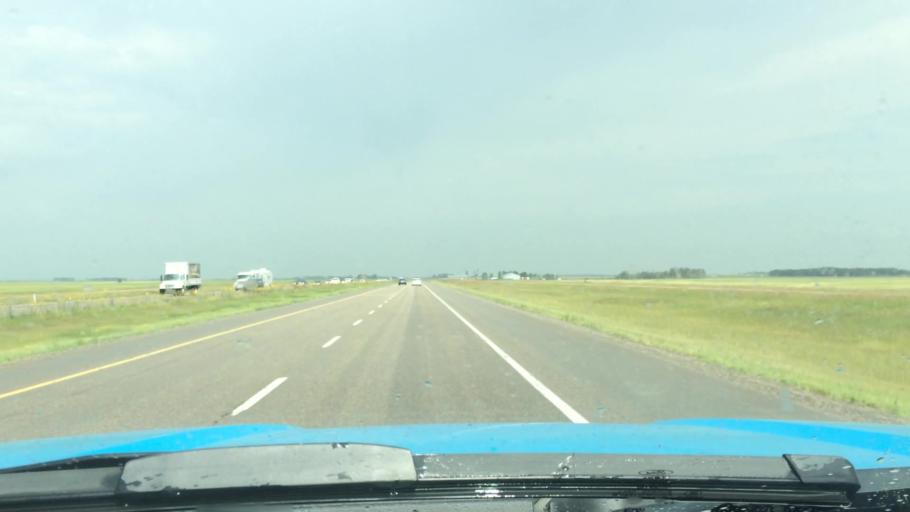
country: CA
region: Alberta
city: Didsbury
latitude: 51.6910
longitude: -114.0253
